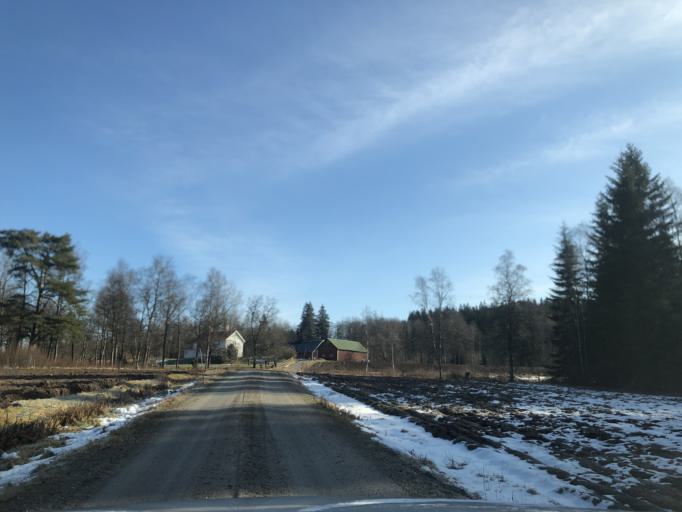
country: SE
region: Vaestra Goetaland
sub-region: Ulricehamns Kommun
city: Ulricehamn
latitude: 57.7924
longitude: 13.4833
